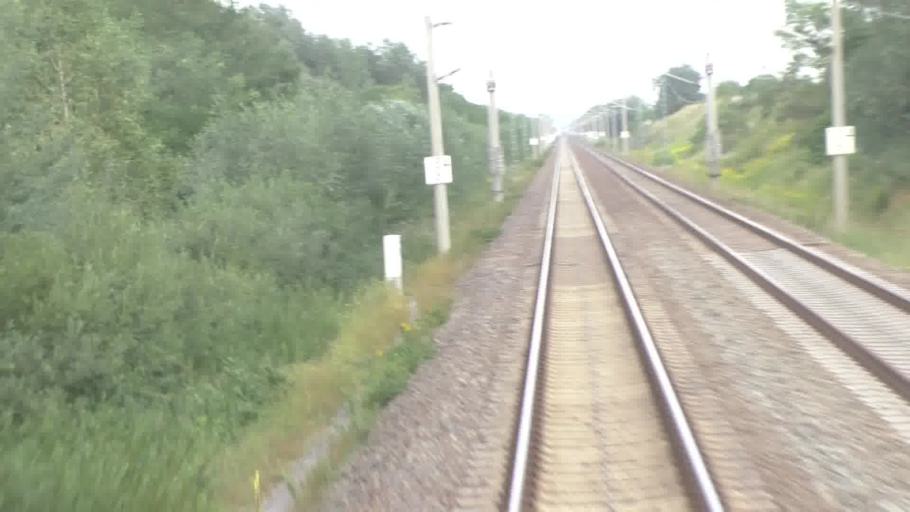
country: DE
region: Brandenburg
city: Kotzen
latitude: 52.5945
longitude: 12.5897
